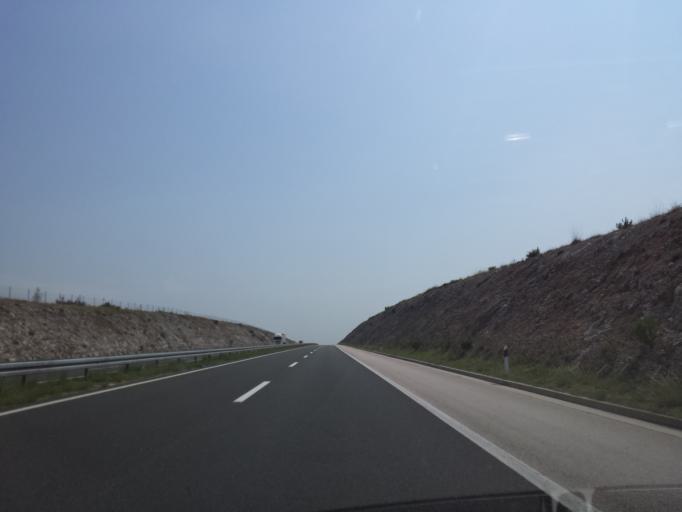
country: HR
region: Zadarska
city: Polaca
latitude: 44.0775
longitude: 15.5118
